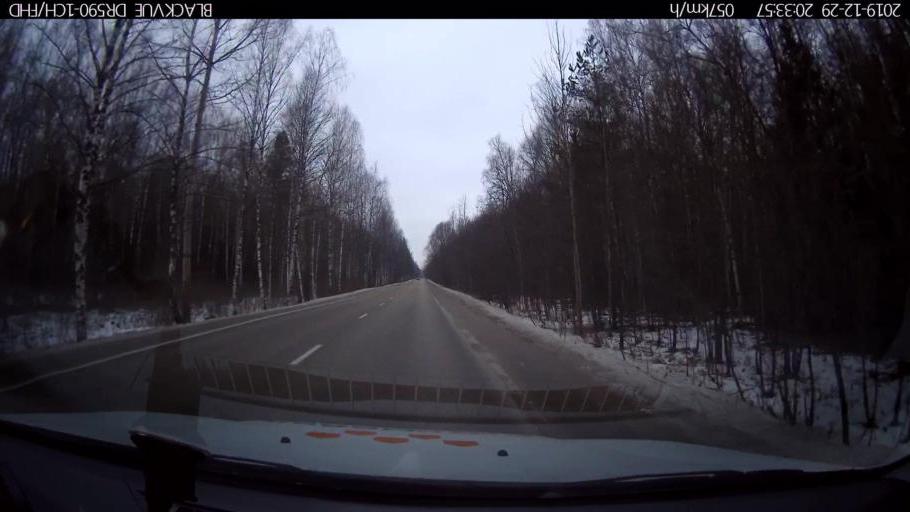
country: RU
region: Nizjnij Novgorod
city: Afonino
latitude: 56.1833
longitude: 44.0456
